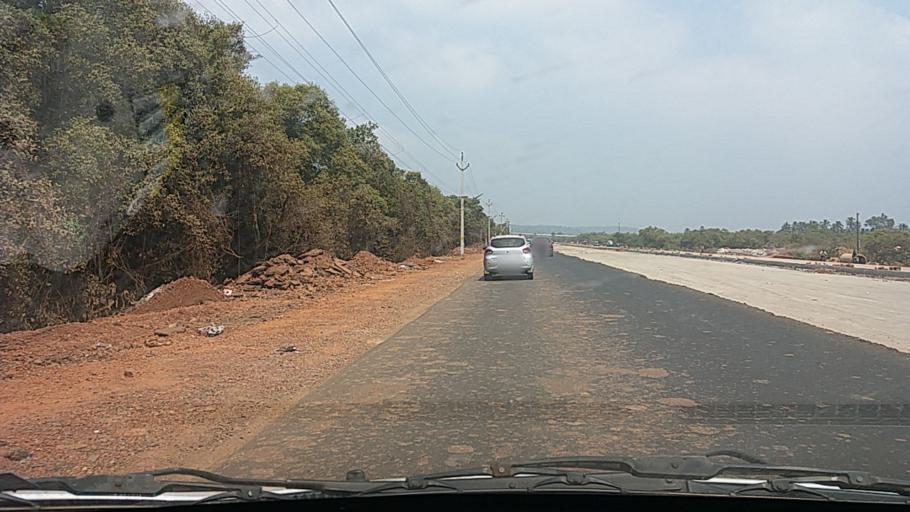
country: IN
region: Goa
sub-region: North Goa
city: Taleigao
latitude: 15.4829
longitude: 73.8472
